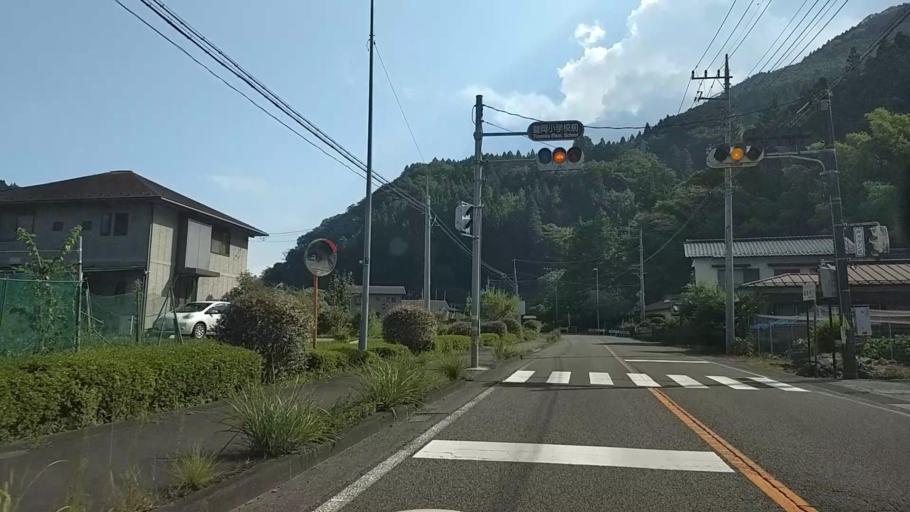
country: JP
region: Shizuoka
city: Fujinomiya
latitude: 35.3512
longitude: 138.4218
